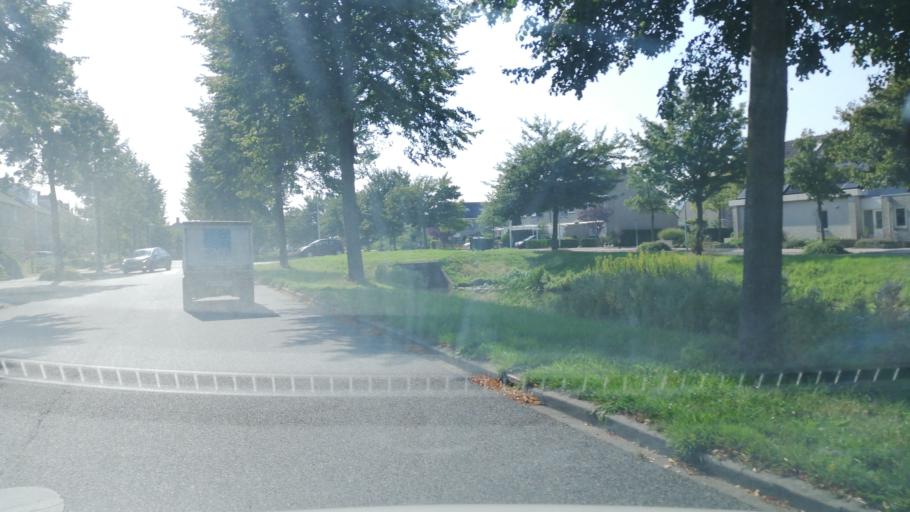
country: NL
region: Overijssel
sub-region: Gemeente Zwolle
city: Zwolle
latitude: 52.4942
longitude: 6.0986
